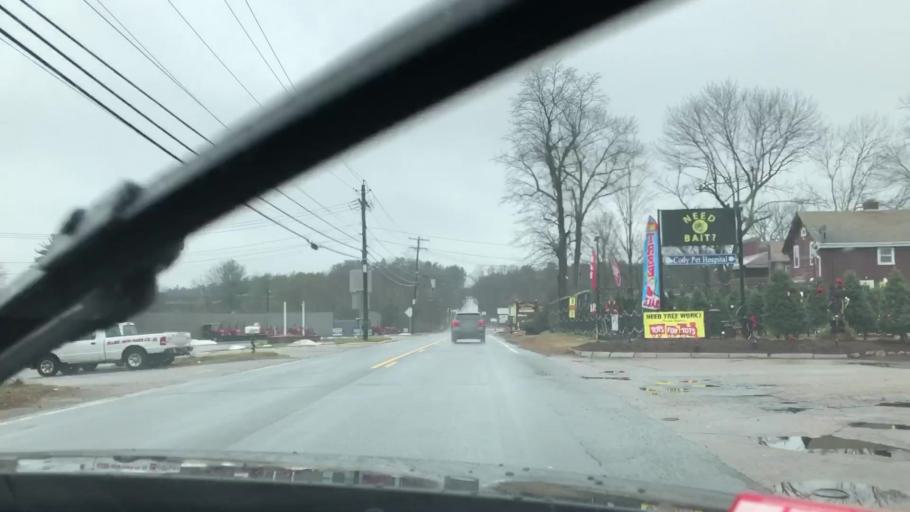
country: US
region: Massachusetts
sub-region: Norfolk County
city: Wrentham
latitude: 42.0889
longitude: -71.3016
